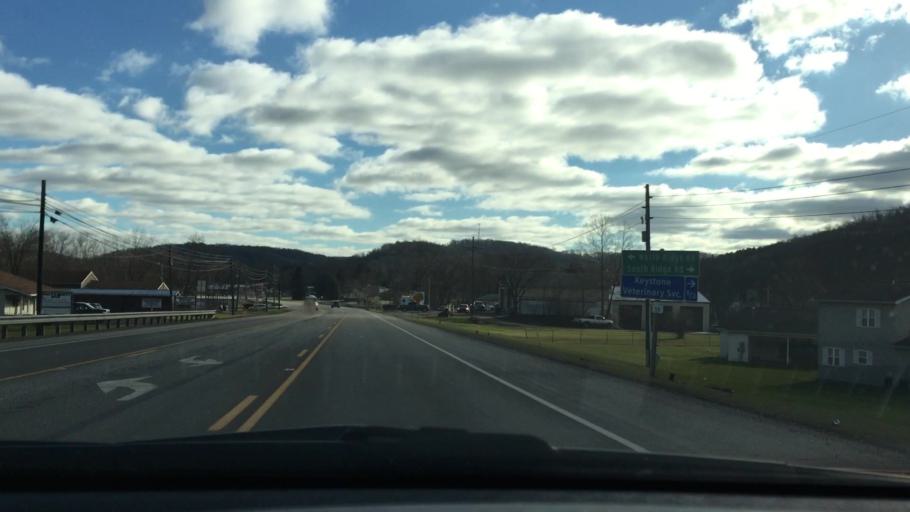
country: US
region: Pennsylvania
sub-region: Indiana County
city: Indiana
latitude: 40.6553
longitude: -79.2946
